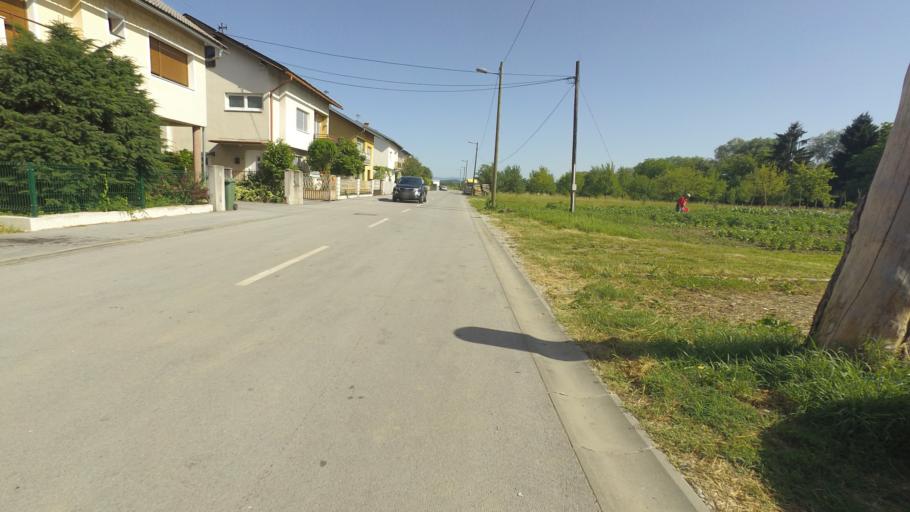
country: HR
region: Karlovacka
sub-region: Grad Karlovac
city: Karlovac
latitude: 45.4991
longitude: 15.5427
